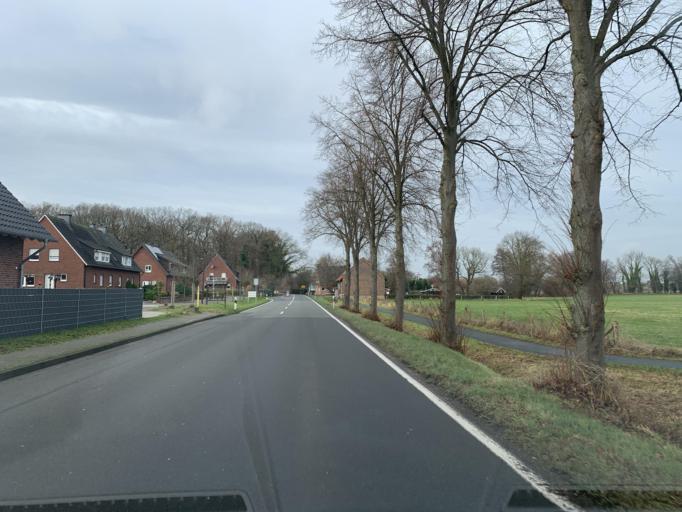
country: DE
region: North Rhine-Westphalia
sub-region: Regierungsbezirk Munster
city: Ascheberg
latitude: 51.8208
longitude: 7.5891
